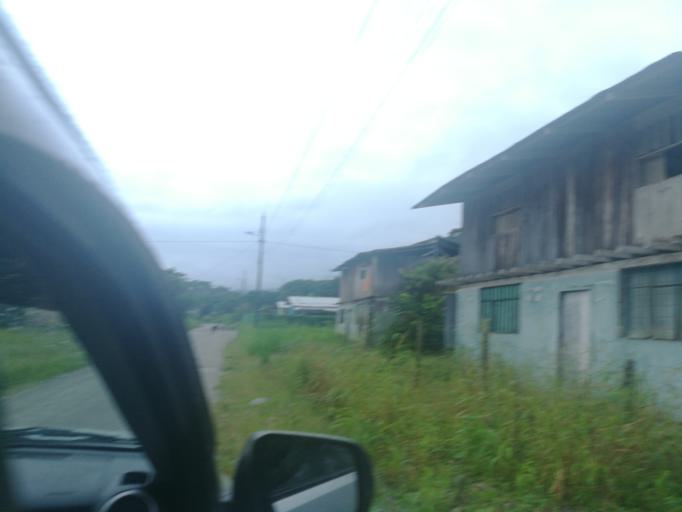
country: EC
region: Napo
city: Tena
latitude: -1.0388
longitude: -77.6599
